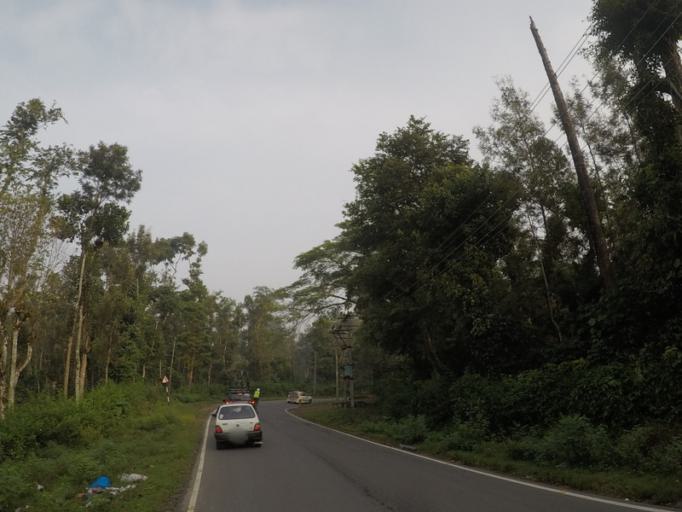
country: IN
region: Karnataka
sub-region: Chikmagalur
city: Mudigere
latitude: 13.2544
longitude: 75.6386
